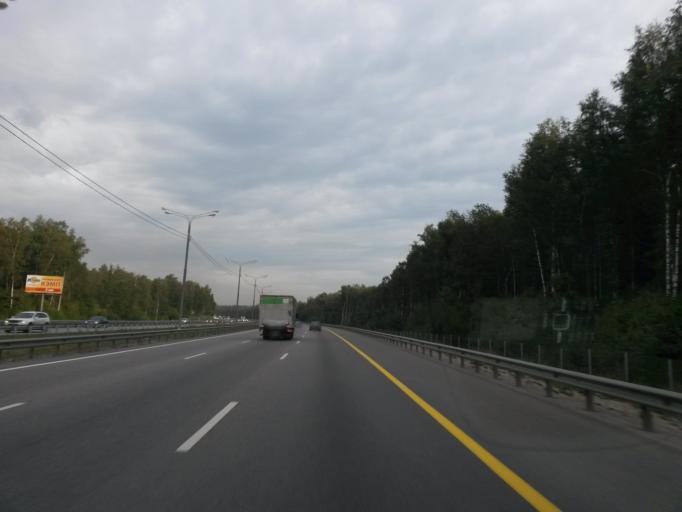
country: RU
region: Moskovskaya
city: Vostryakovo
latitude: 55.3528
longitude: 37.8045
